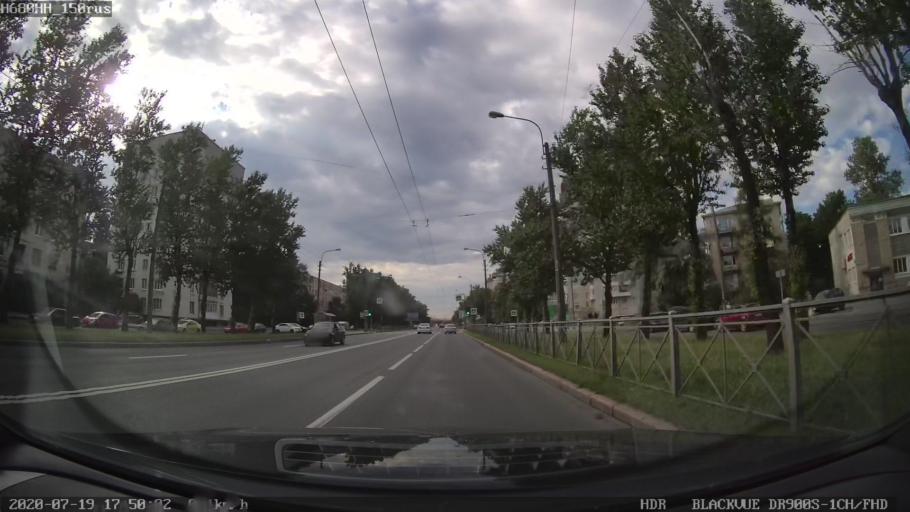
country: RU
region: St.-Petersburg
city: Avtovo
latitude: 59.8547
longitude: 30.2974
